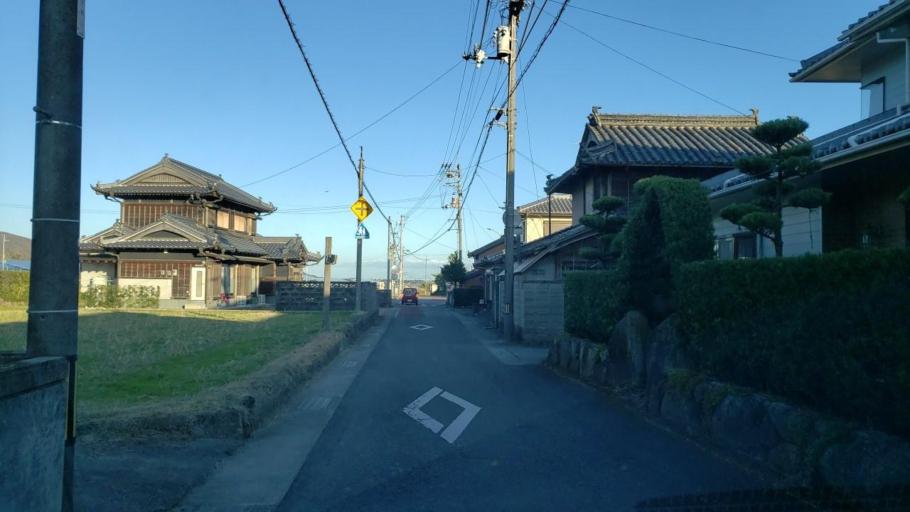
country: JP
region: Tokushima
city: Wakimachi
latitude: 34.0913
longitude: 134.2474
